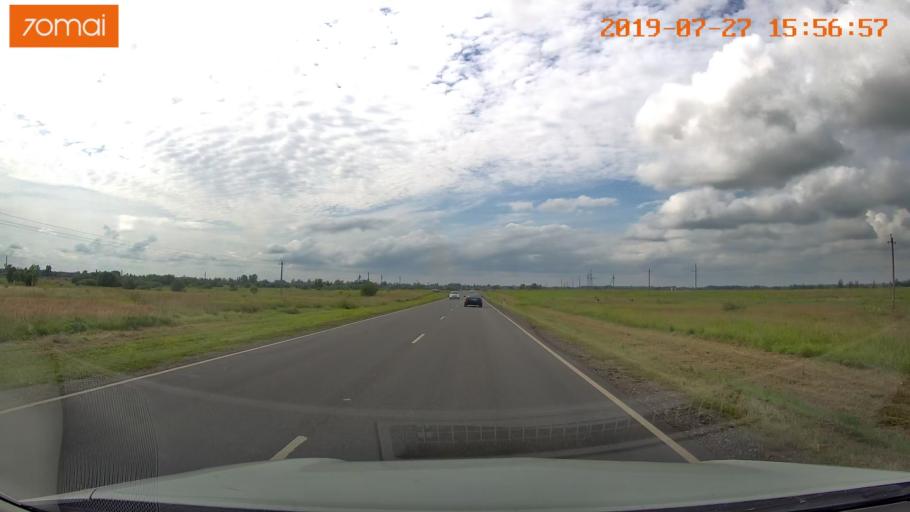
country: RU
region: Kaliningrad
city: Chernyakhovsk
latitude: 54.6214
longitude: 21.8923
